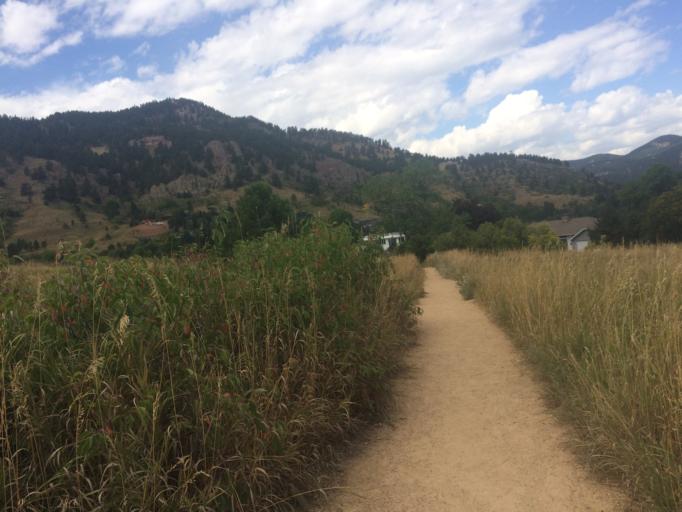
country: US
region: Colorado
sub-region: Boulder County
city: Boulder
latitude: 39.9994
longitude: -105.2855
